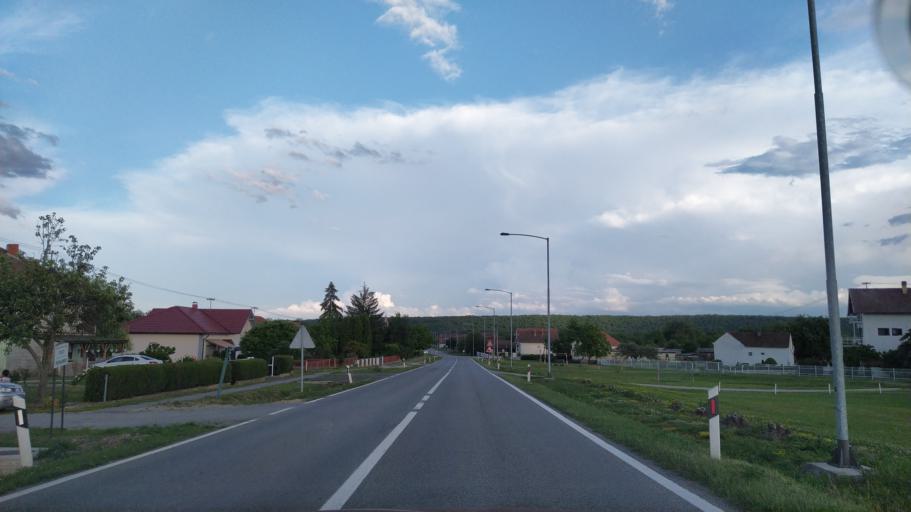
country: HR
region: Osjecko-Baranjska
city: Fericanci
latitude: 45.4998
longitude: 18.0132
